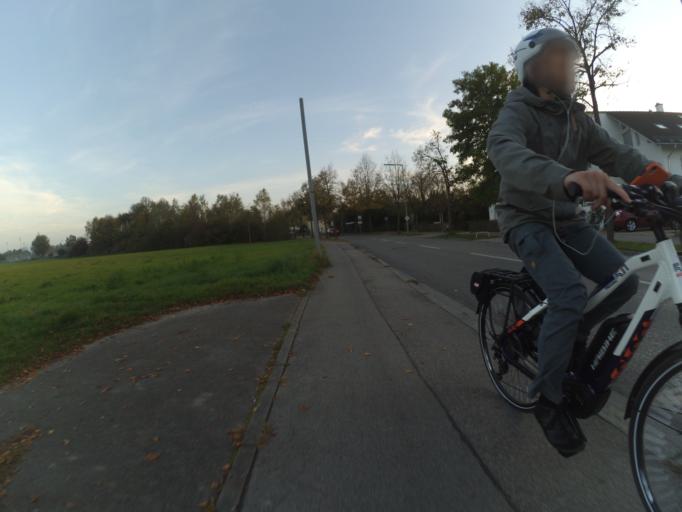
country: DE
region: Bavaria
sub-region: Upper Bavaria
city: Oberschleissheim
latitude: 48.2081
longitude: 11.5332
